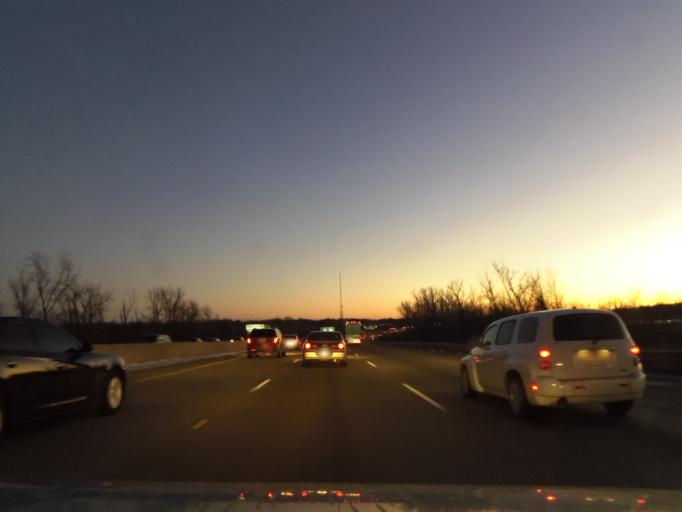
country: US
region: Indiana
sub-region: Lake County
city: New Chicago
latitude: 41.5389
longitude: -87.3110
